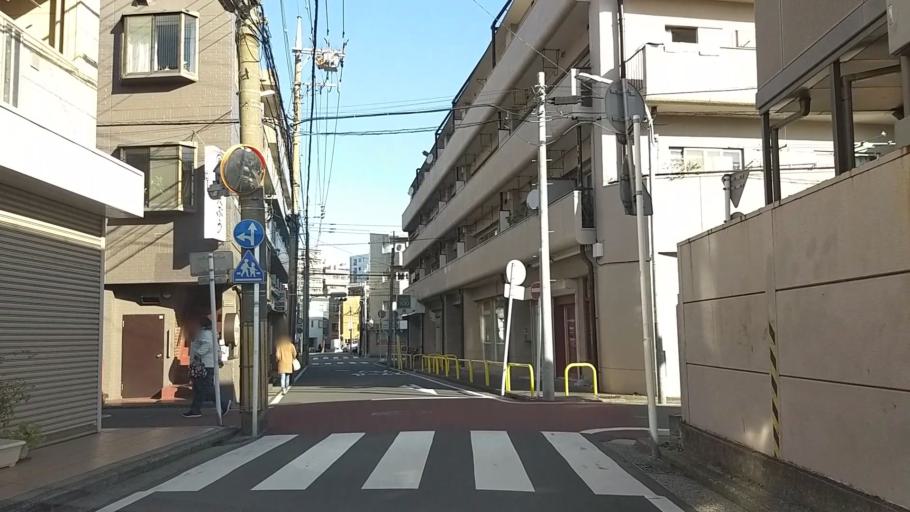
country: JP
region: Kanagawa
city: Yokohama
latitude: 35.4291
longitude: 139.6126
